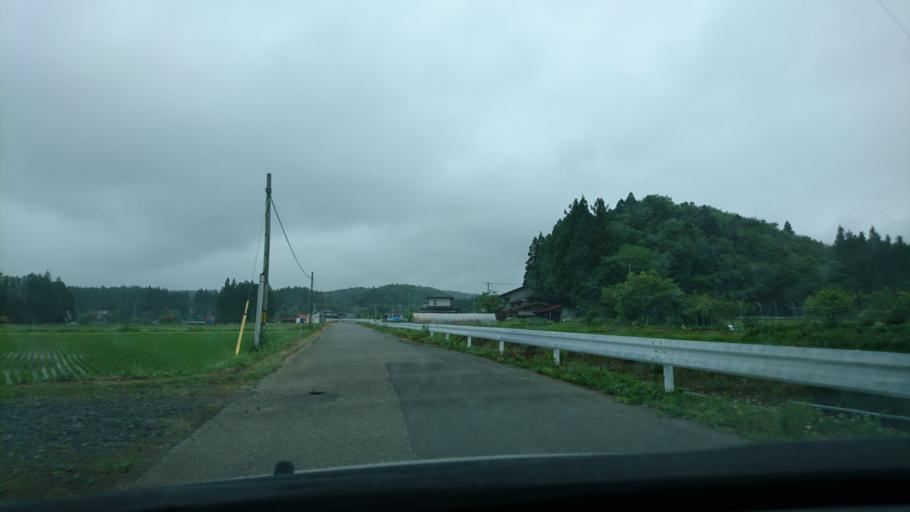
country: JP
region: Iwate
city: Ichinoseki
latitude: 38.9513
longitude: 141.0420
